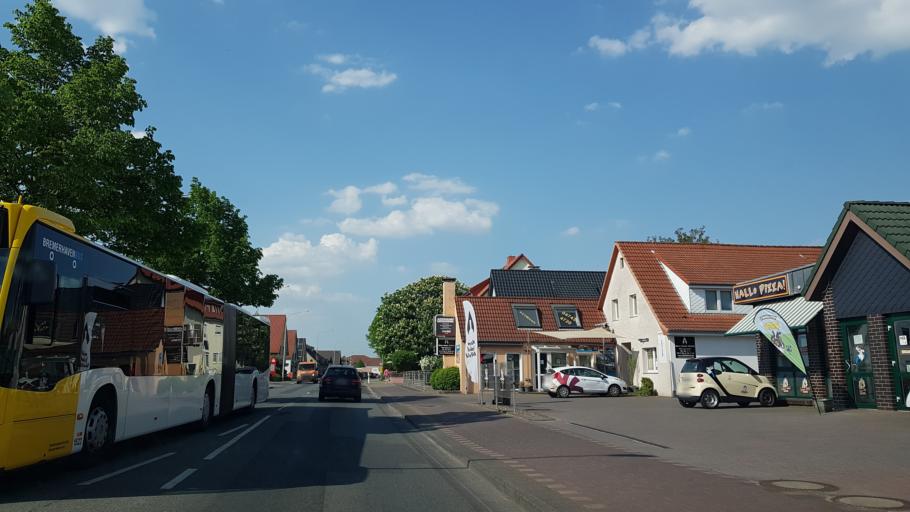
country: DE
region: Lower Saxony
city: Langen
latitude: 53.6040
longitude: 8.5949
